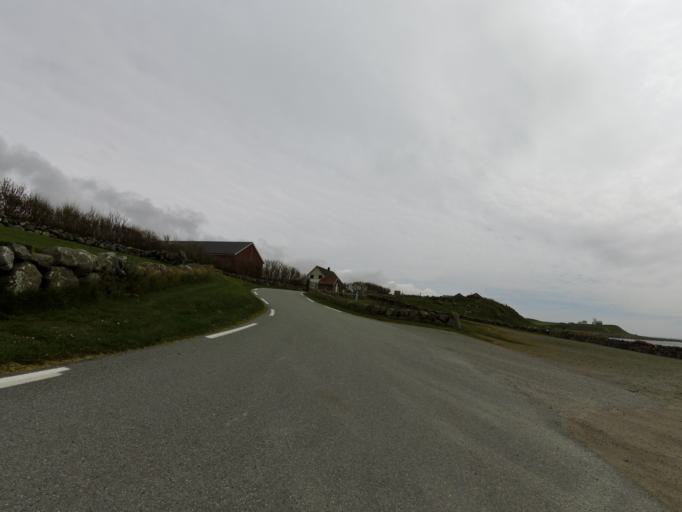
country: NO
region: Rogaland
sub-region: Ha
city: Naerbo
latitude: 58.6666
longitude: 5.5511
